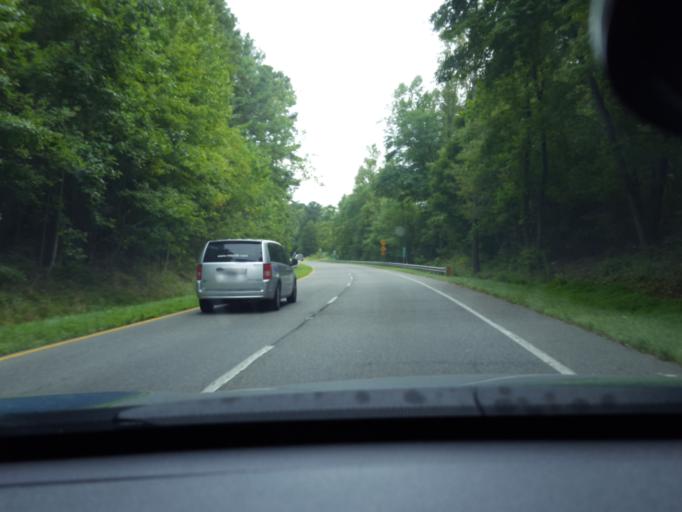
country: US
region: Virginia
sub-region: Caroline County
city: Bowling Green
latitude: 38.0552
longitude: -77.3432
